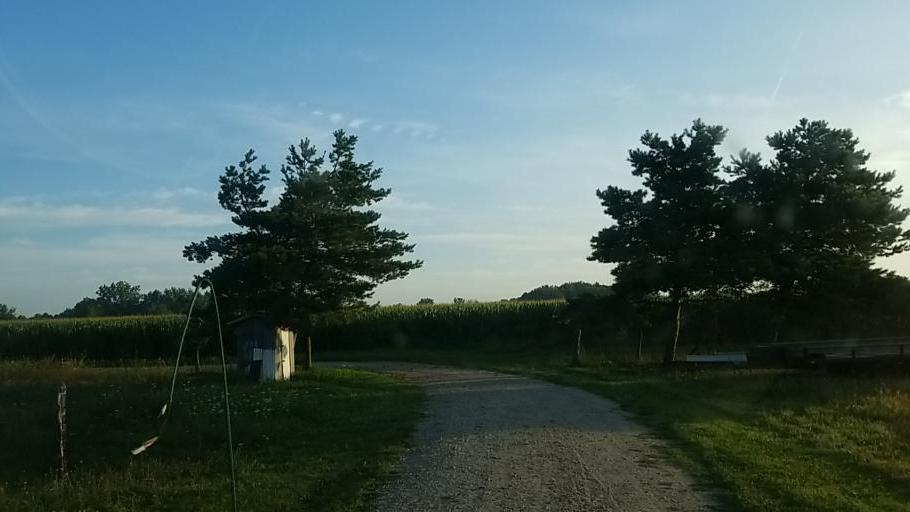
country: US
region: Michigan
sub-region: Montcalm County
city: Howard City
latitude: 43.3449
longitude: -85.3994
